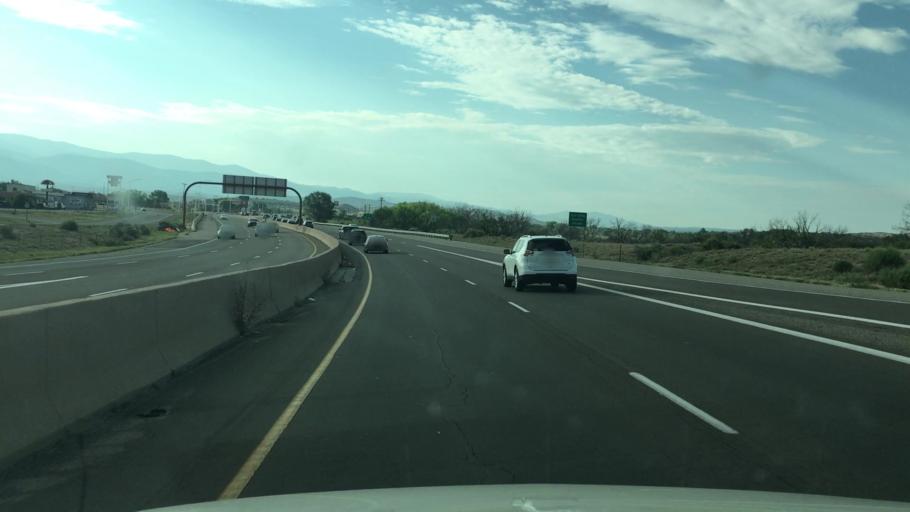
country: US
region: New Mexico
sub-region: Santa Fe County
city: Pojoaque
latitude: 35.8882
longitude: -106.0214
